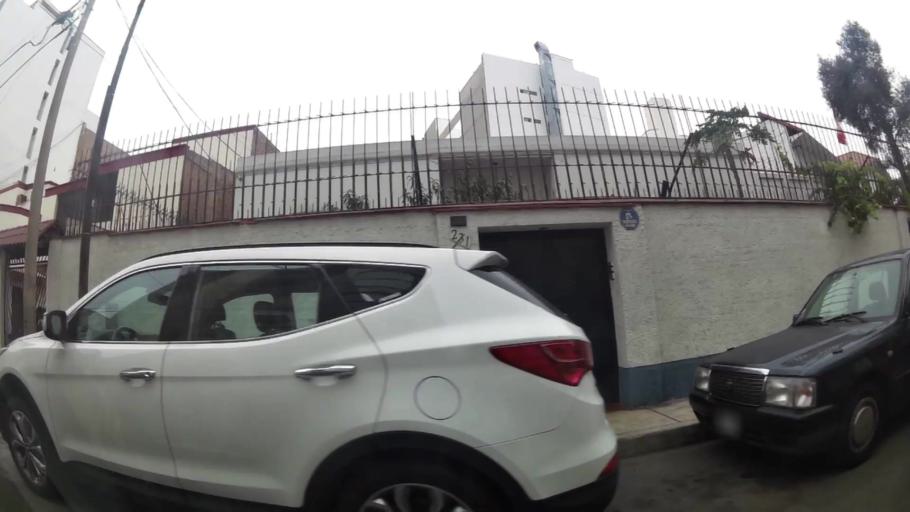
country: PE
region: Lima
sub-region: Lima
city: San Isidro
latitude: -12.1286
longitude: -77.0342
